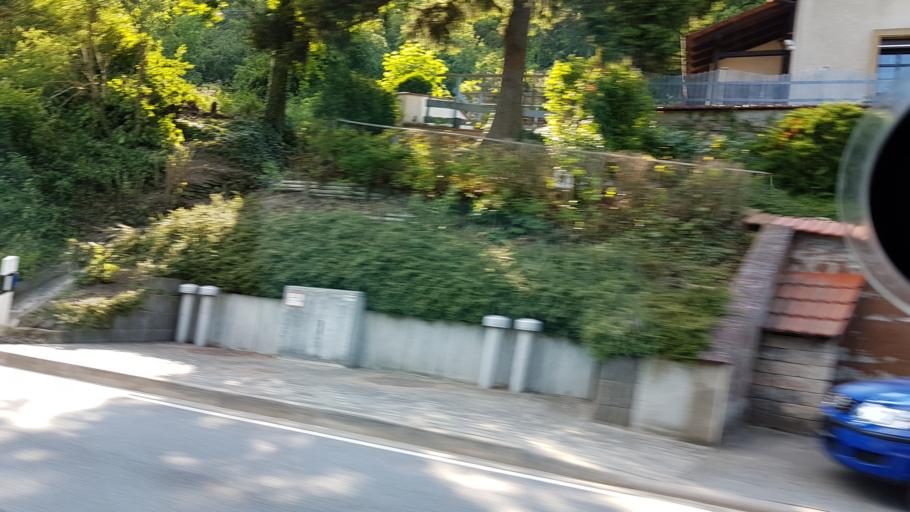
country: DE
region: Rheinland-Pfalz
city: Medard
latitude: 49.6718
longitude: 7.6192
